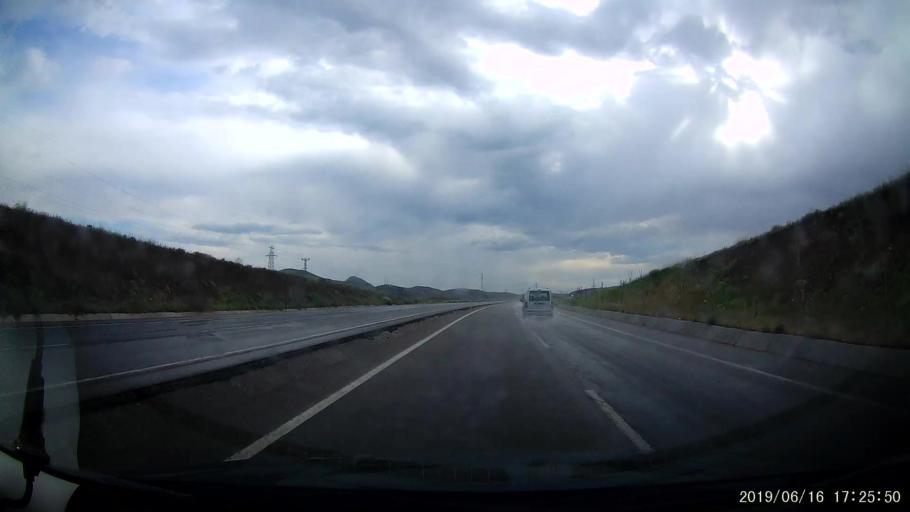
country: TR
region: Erzincan
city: Tercan
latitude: 39.7669
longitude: 40.4267
